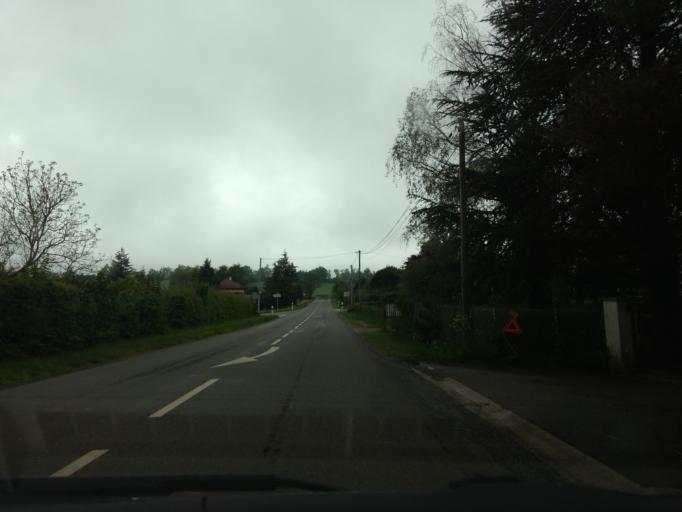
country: FR
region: Midi-Pyrenees
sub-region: Departement de l'Aveyron
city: Montbazens
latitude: 44.4594
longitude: 2.2278
